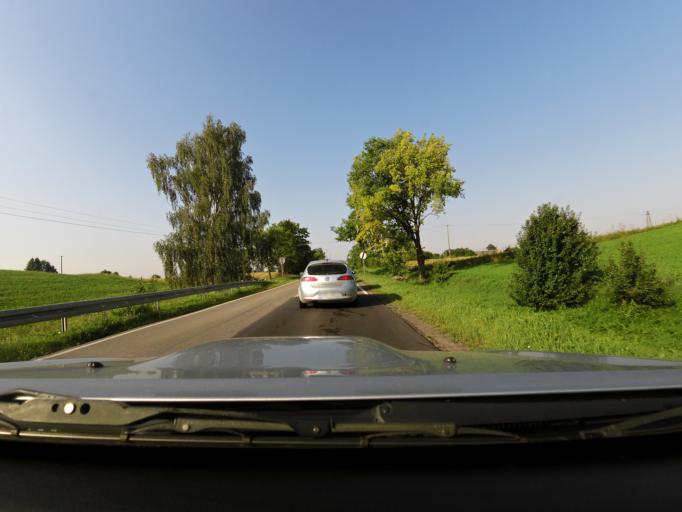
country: PL
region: Podlasie
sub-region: Powiat sejnenski
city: Sejny
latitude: 54.1119
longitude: 23.4218
